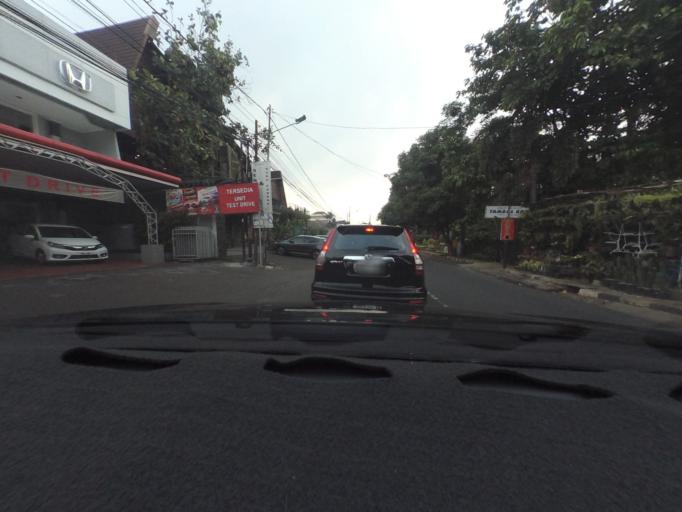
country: ID
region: West Java
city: Bogor
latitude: -6.6026
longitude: 106.8110
